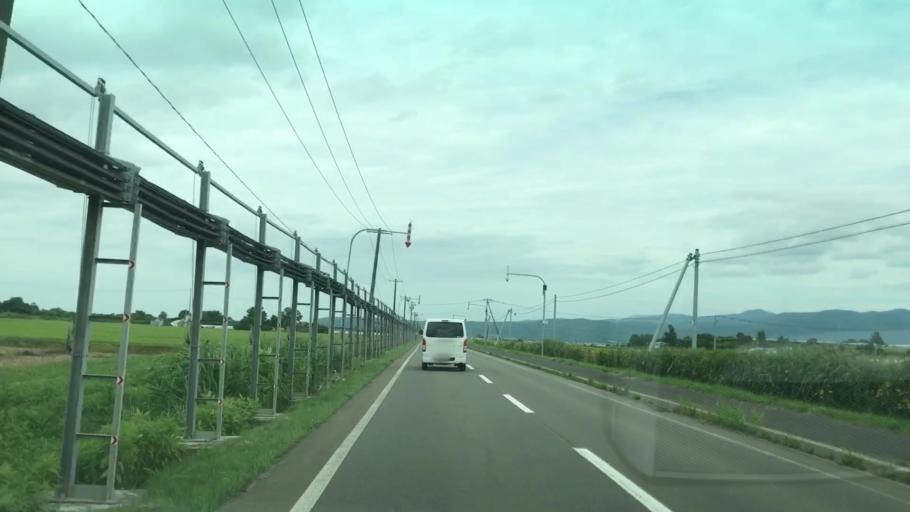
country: JP
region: Hokkaido
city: Iwanai
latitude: 42.9953
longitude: 140.5976
